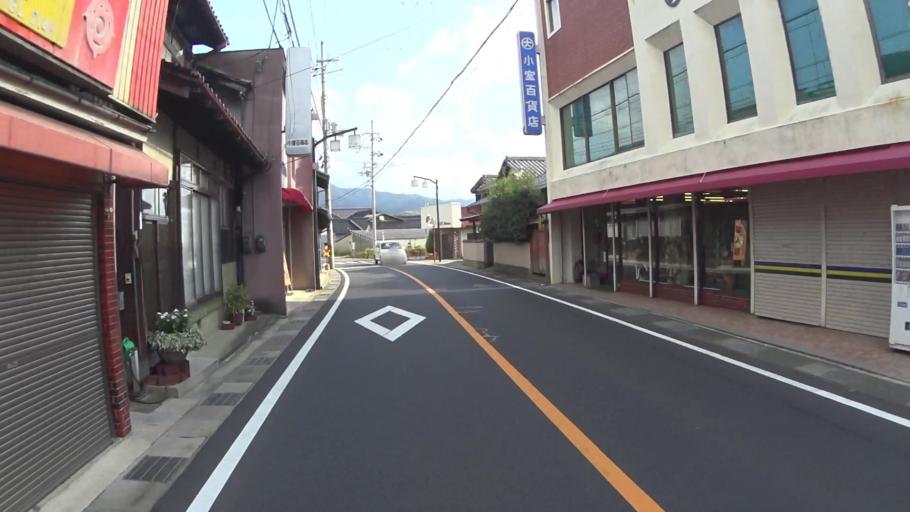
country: JP
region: Kyoto
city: Miyazu
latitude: 35.5660
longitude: 135.1528
